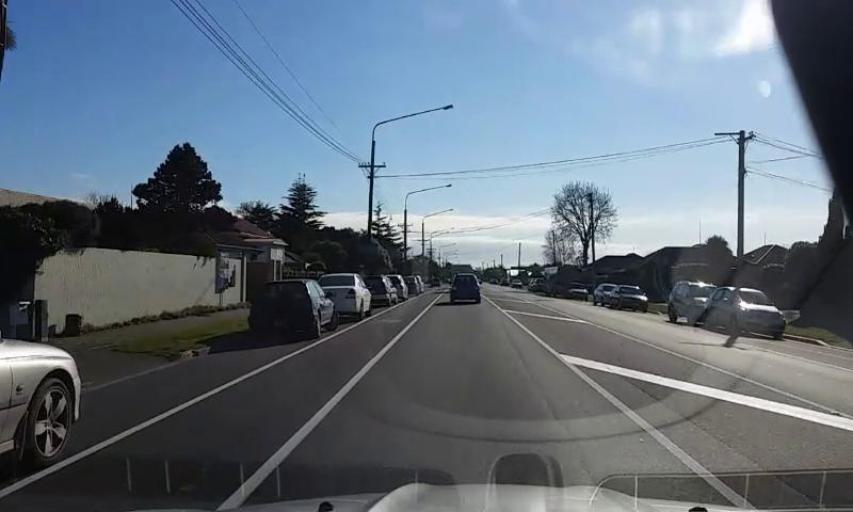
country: NZ
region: Canterbury
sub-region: Christchurch City
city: Christchurch
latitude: -43.5046
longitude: 172.6625
